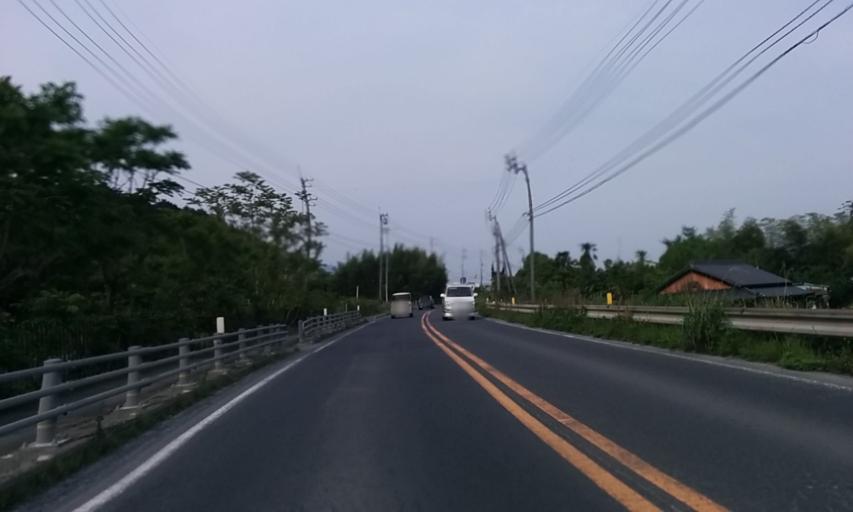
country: JP
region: Ehime
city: Niihama
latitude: 33.9588
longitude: 133.4420
